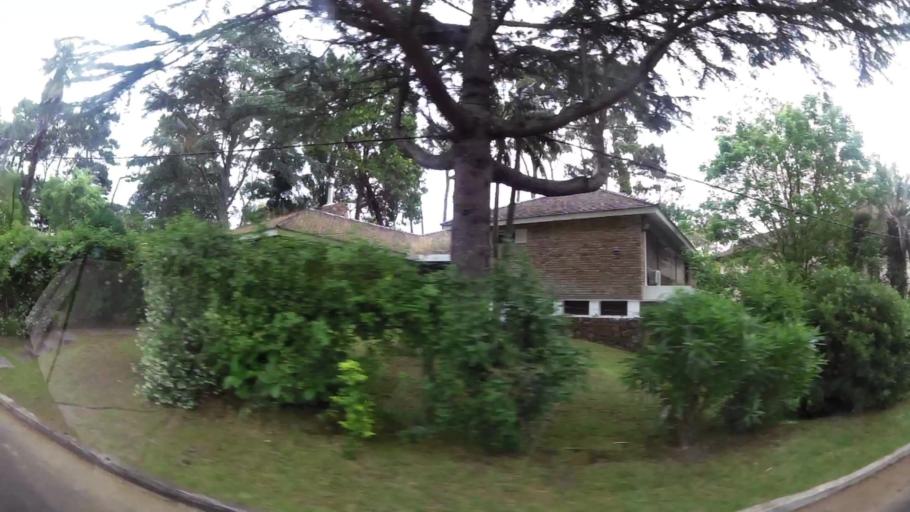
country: UY
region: Maldonado
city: Maldonado
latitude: -34.9236
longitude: -54.9546
